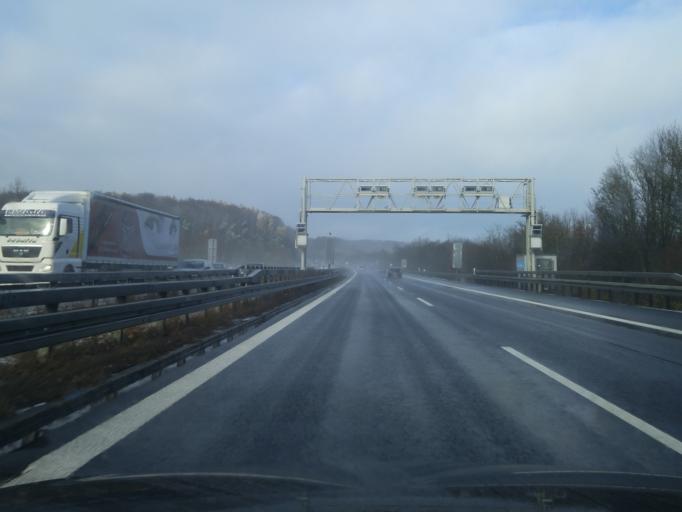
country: DE
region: Bavaria
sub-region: Regierungsbezirk Unterfranken
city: Wasserlosen
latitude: 50.0894
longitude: 9.9846
